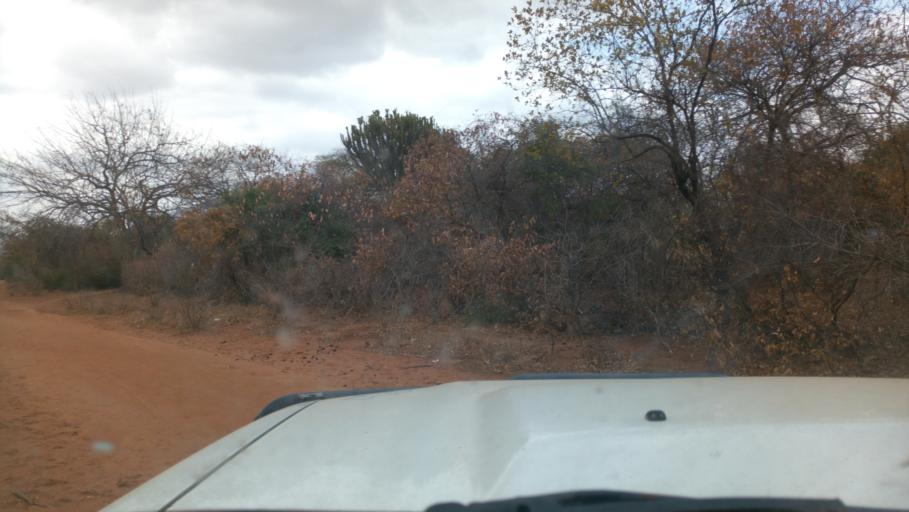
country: KE
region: Kitui
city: Kitui
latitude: -1.8506
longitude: 38.3476
